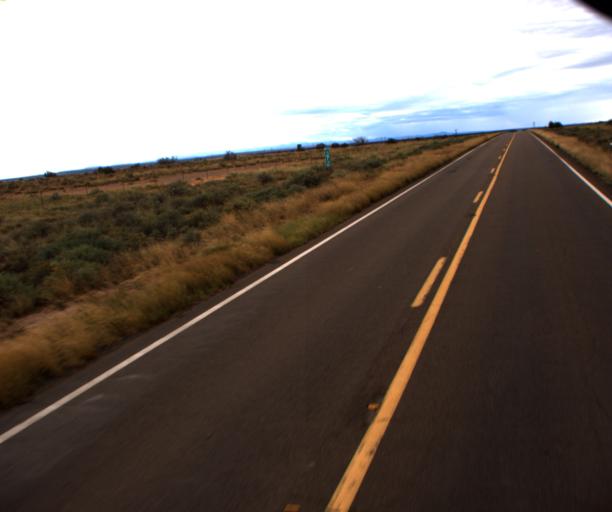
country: US
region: Arizona
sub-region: Navajo County
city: Snowflake
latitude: 34.6698
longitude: -110.1018
